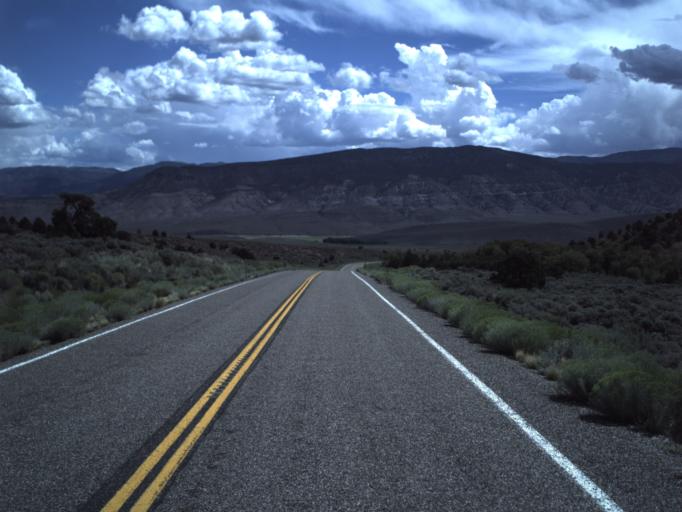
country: US
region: Utah
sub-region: Piute County
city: Junction
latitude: 38.2607
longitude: -112.2570
